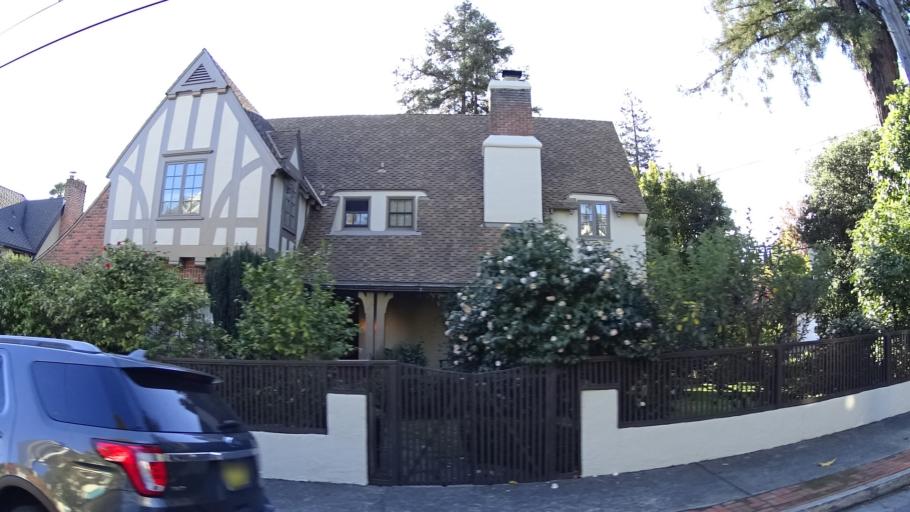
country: US
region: California
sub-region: Alameda County
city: Piedmont
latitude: 37.8135
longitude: -122.2228
